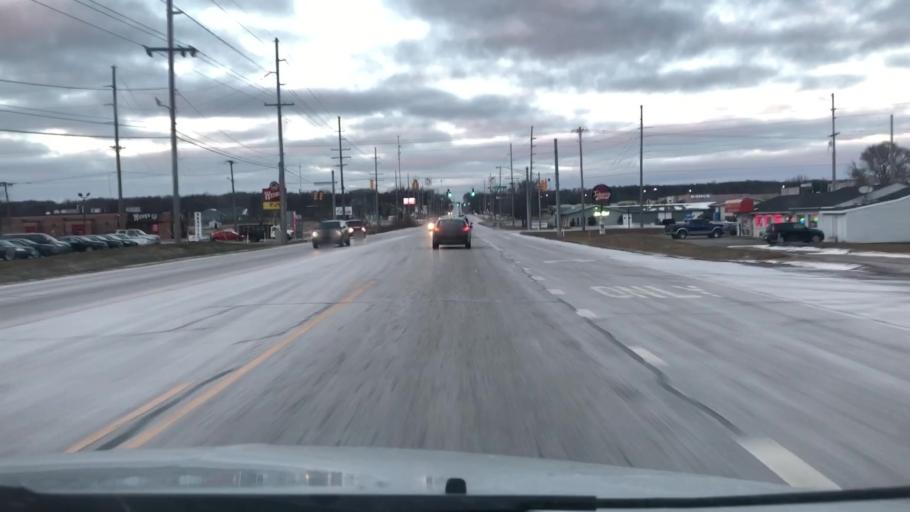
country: US
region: Indiana
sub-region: Steuben County
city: Angola
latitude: 41.6709
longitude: -84.9996
